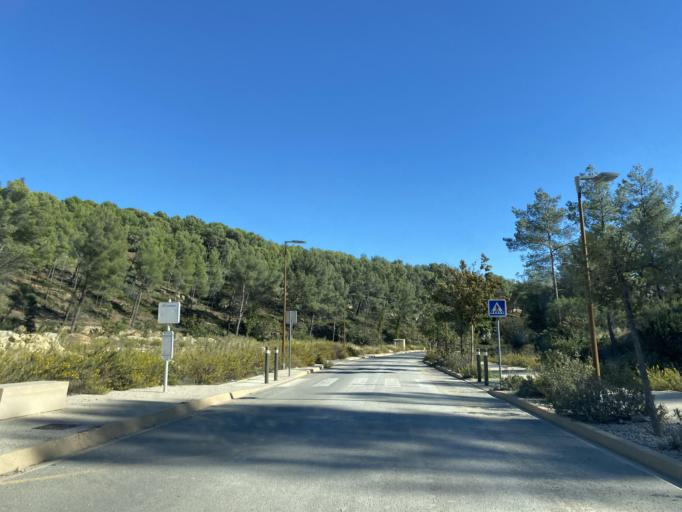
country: FR
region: Provence-Alpes-Cote d'Azur
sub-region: Departement des Bouches-du-Rhone
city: Ceyreste
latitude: 43.2118
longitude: 5.6015
